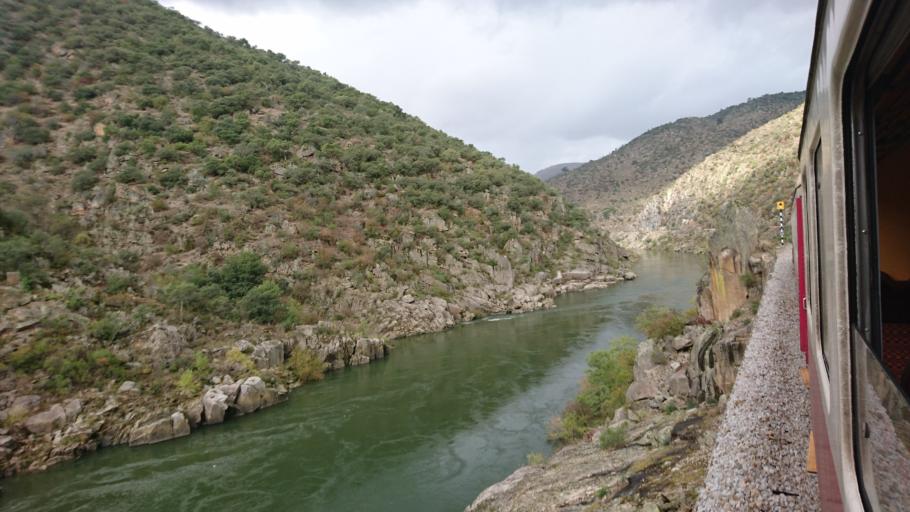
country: PT
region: Viseu
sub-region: Sao Joao da Pesqueira
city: Sao Joao da Pesqueira
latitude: 41.1898
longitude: -7.3872
